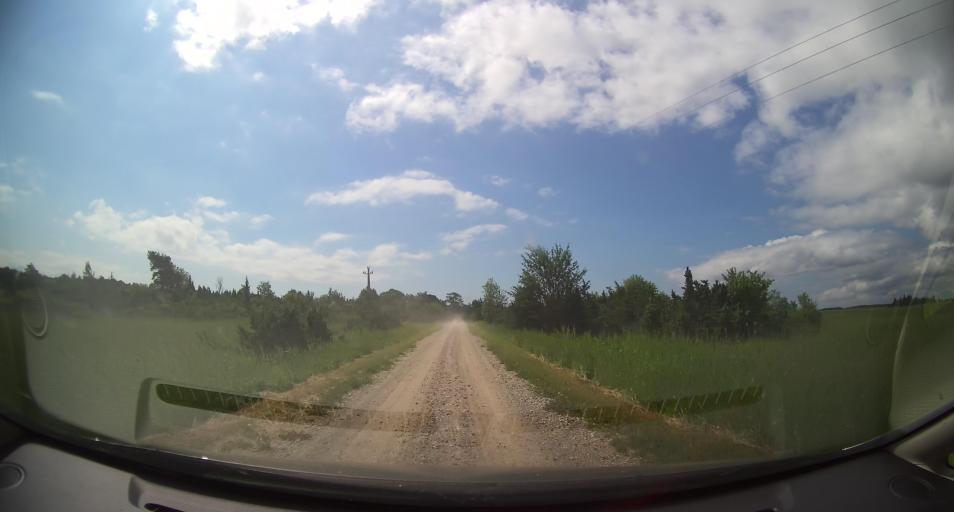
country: EE
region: Laeaene
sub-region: Lihula vald
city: Lihula
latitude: 58.5675
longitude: 23.5468
